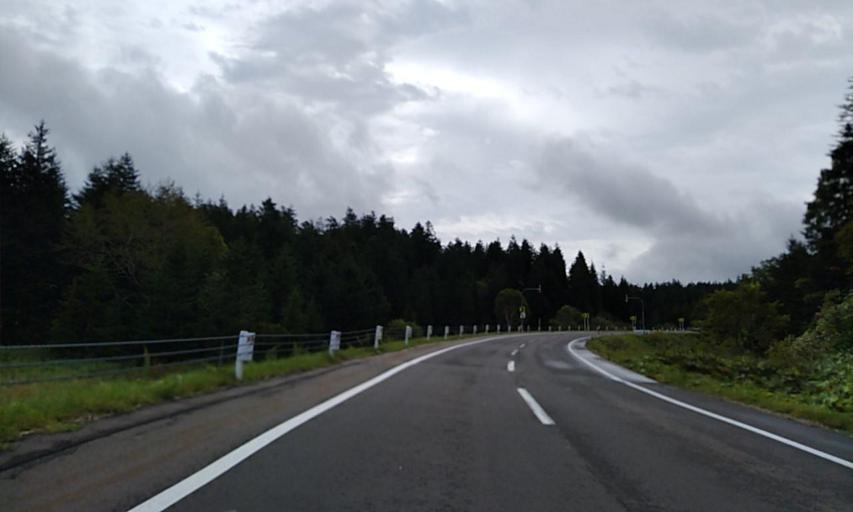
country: JP
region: Hokkaido
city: Abashiri
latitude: 43.6240
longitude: 144.5789
